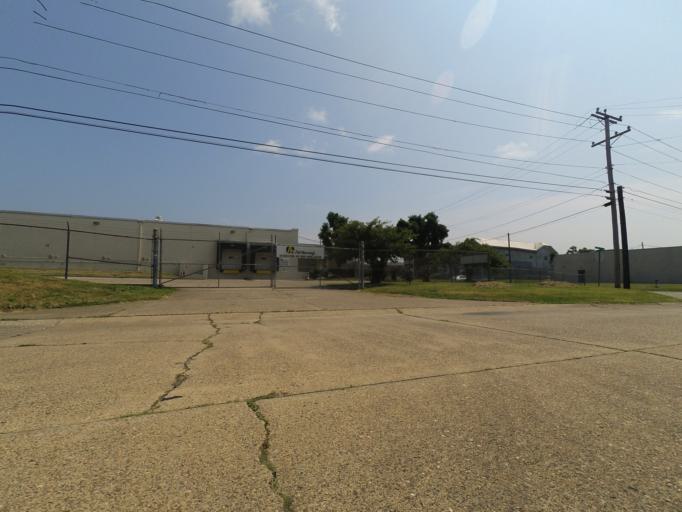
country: US
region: West Virginia
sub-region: Cabell County
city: Huntington
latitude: 38.4295
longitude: -82.4172
